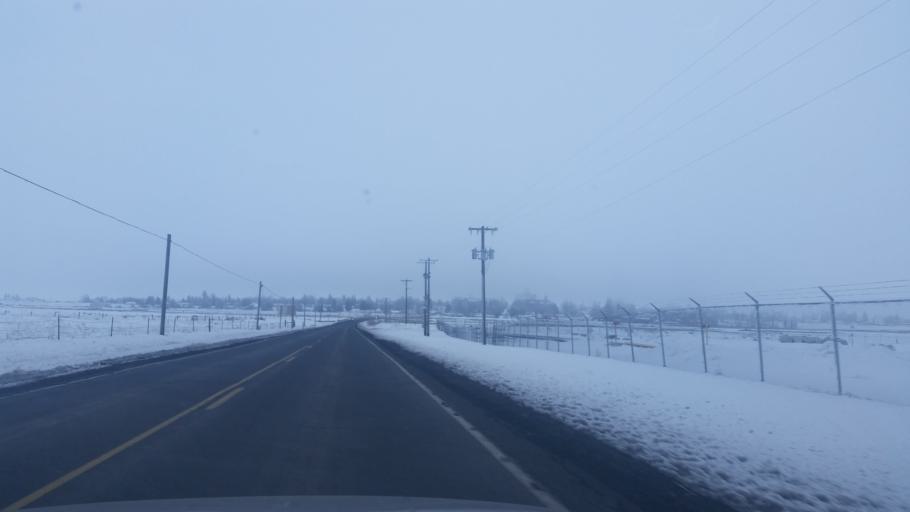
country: US
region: Washington
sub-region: Spokane County
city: Medical Lake
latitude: 47.6813
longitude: -117.8796
